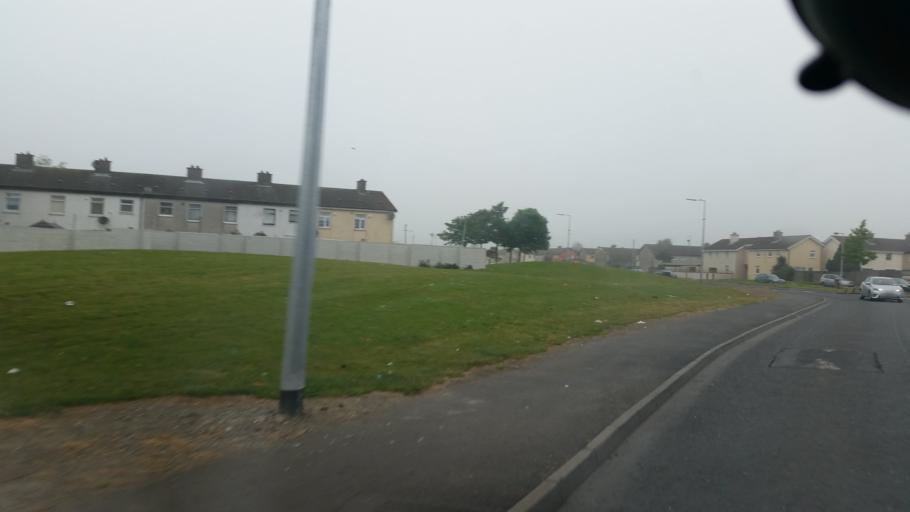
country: IE
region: Leinster
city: Ballymun
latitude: 53.4001
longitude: -6.2771
